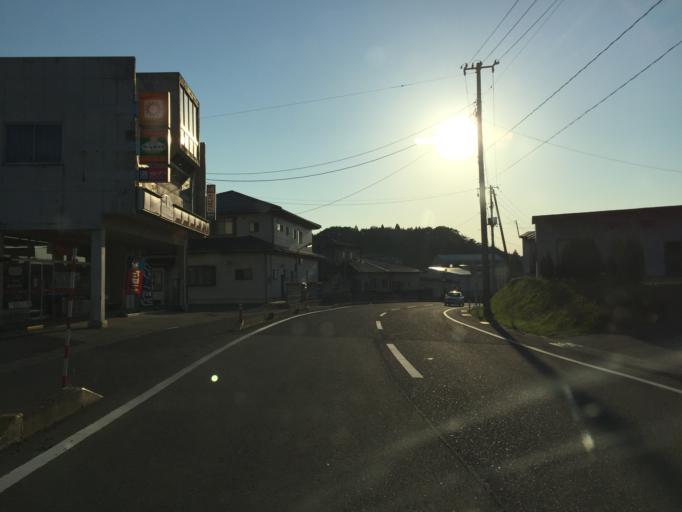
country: JP
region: Fukushima
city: Ishikawa
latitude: 37.1079
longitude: 140.3893
